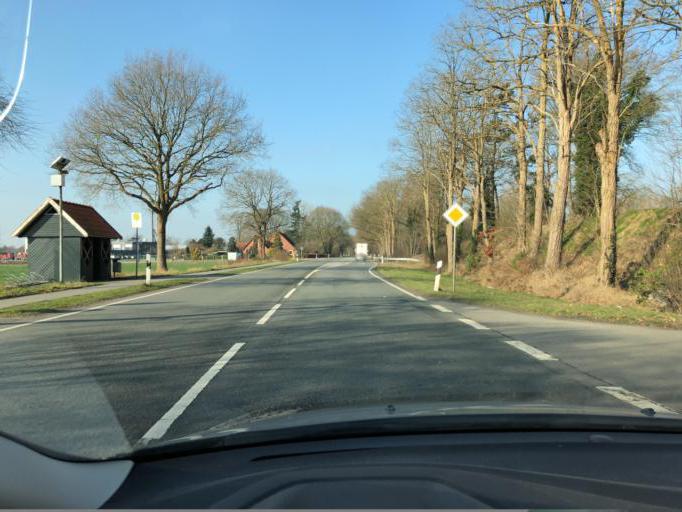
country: DE
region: Lower Saxony
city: Westerstede
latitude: 53.2921
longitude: 7.8760
